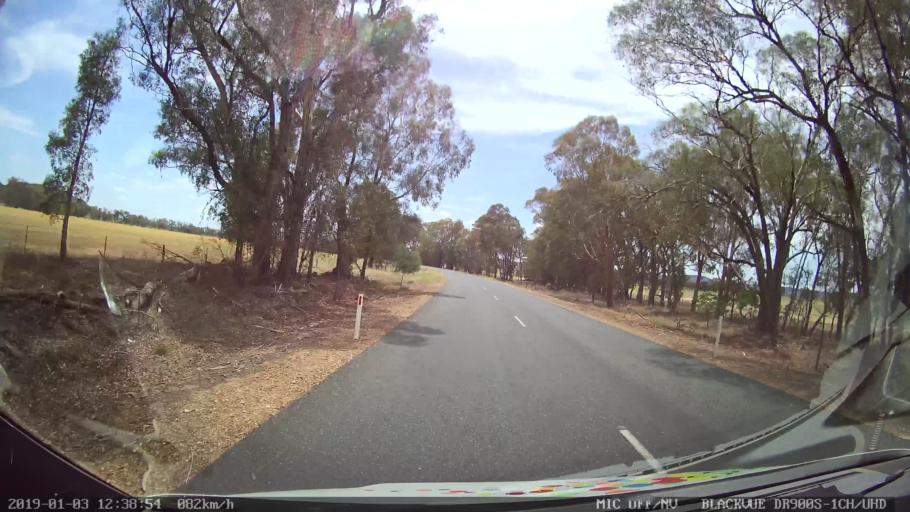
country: AU
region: New South Wales
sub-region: Weddin
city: Grenfell
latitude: -33.8299
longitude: 148.2012
